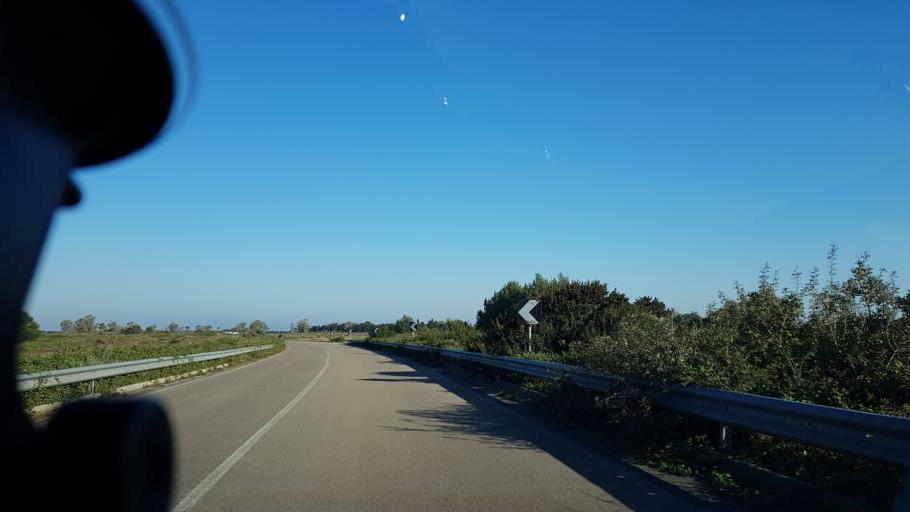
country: IT
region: Apulia
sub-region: Provincia di Lecce
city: Merine
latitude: 40.3947
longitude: 18.2556
